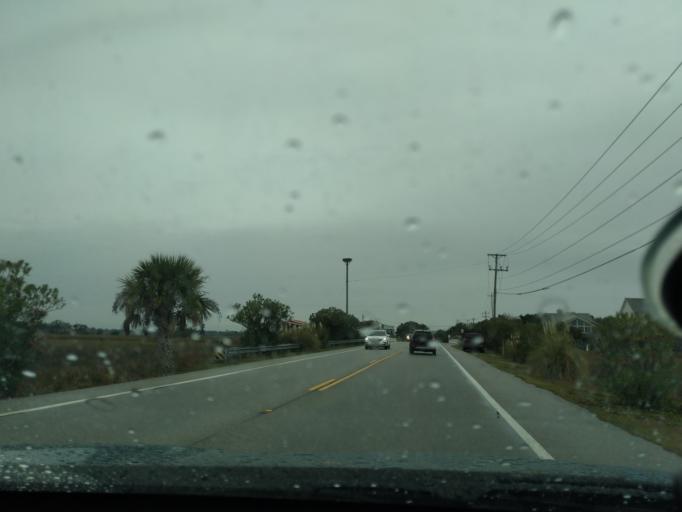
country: US
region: South Carolina
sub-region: Charleston County
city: Folly Beach
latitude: 32.6683
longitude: -79.9467
